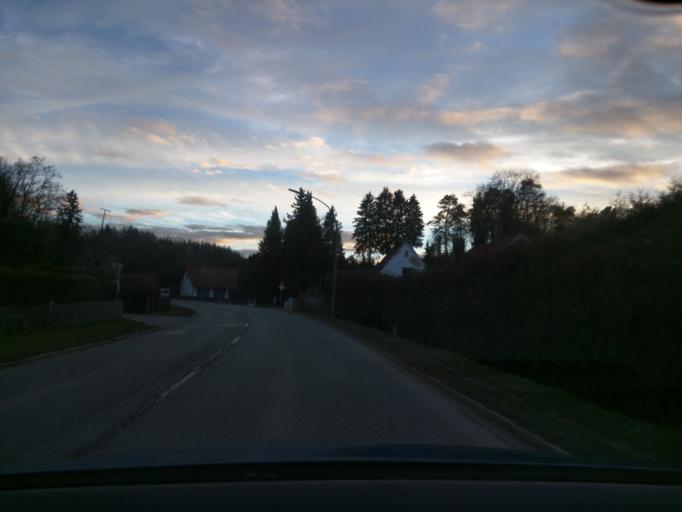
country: DE
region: Bavaria
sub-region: Upper Bavaria
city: Zolling
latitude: 48.4395
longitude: 11.7624
